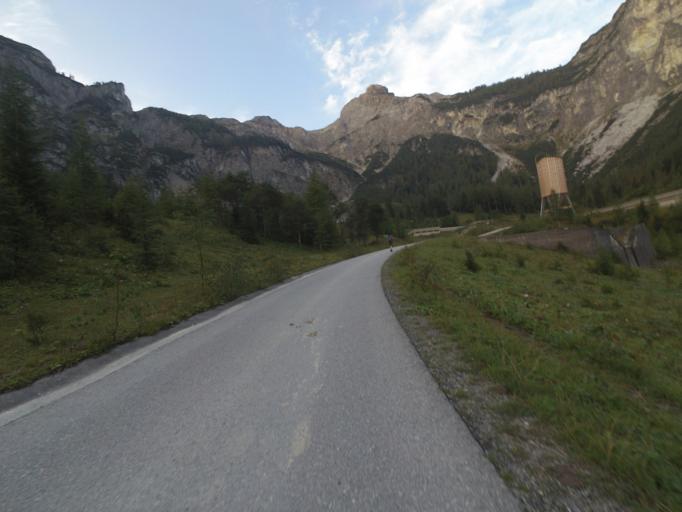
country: AT
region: Salzburg
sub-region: Politischer Bezirk Sankt Johann im Pongau
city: Untertauern
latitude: 47.2391
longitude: 13.4240
